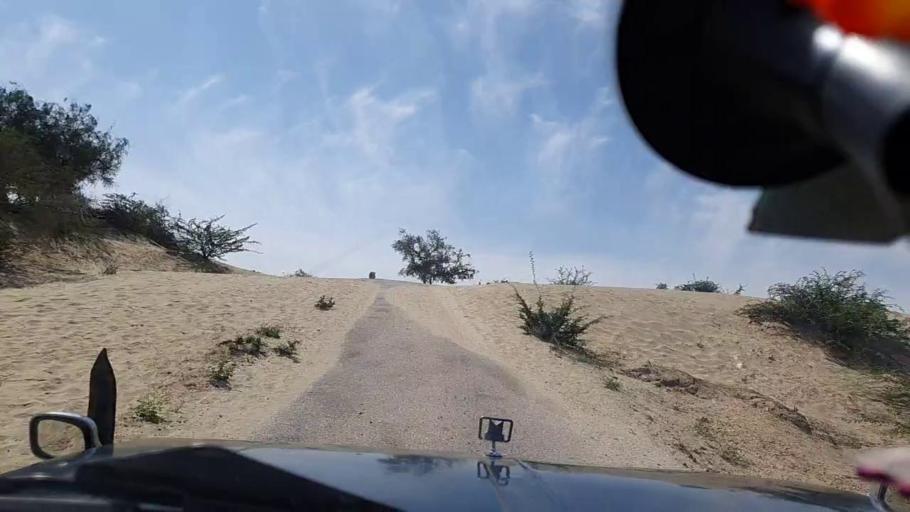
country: PK
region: Sindh
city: Diplo
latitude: 24.3708
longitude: 69.5837
